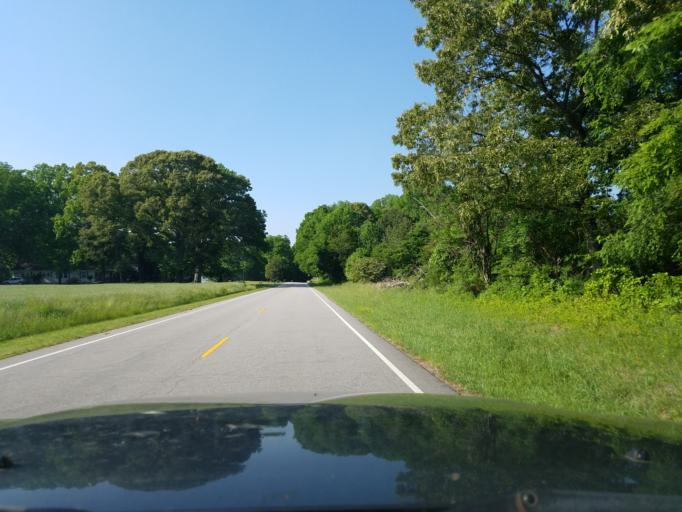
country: US
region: North Carolina
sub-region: Vance County
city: Henderson
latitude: 36.3828
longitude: -78.3690
